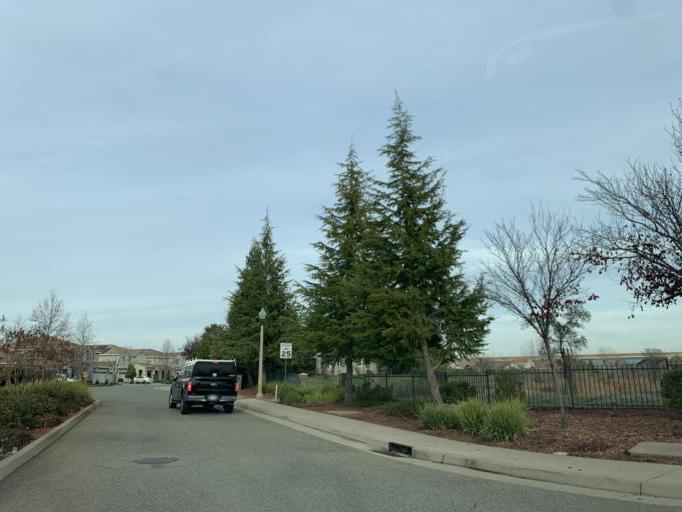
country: US
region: California
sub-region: Placer County
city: Lincoln
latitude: 38.8647
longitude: -121.3090
